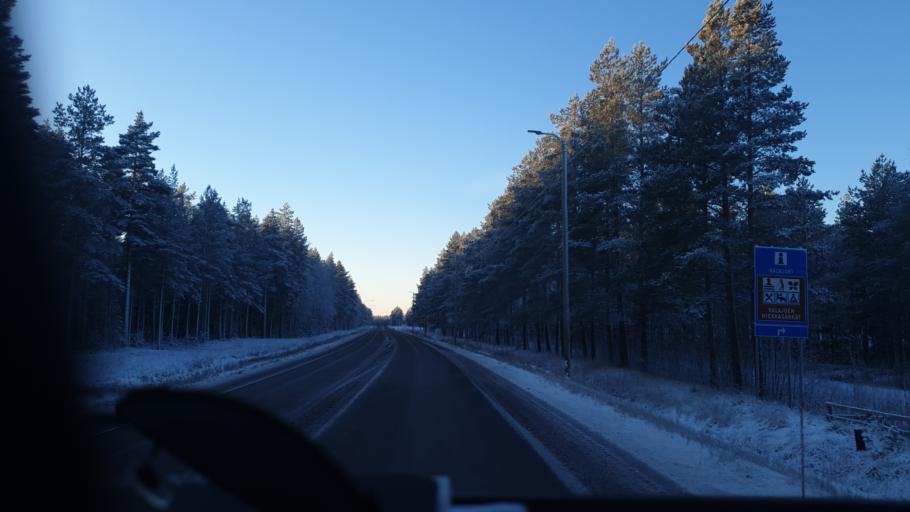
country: FI
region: Northern Ostrobothnia
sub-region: Ylivieska
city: Kalajoki
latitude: 64.2427
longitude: 23.8527
